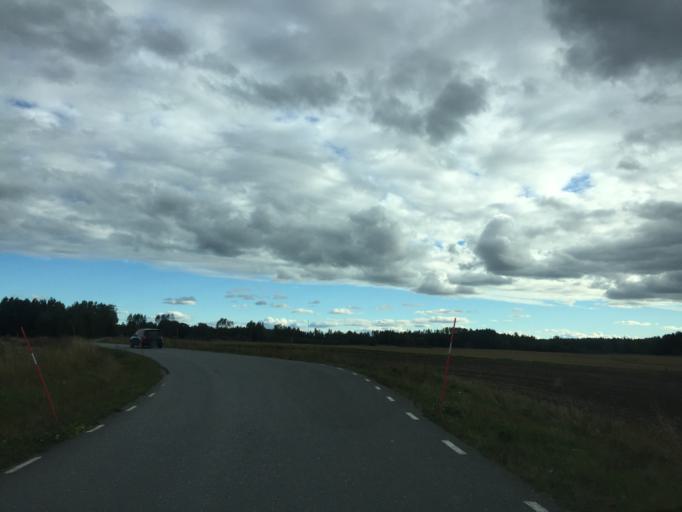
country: SE
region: OErebro
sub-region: Orebro Kommun
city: Hovsta
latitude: 59.3427
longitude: 15.1698
